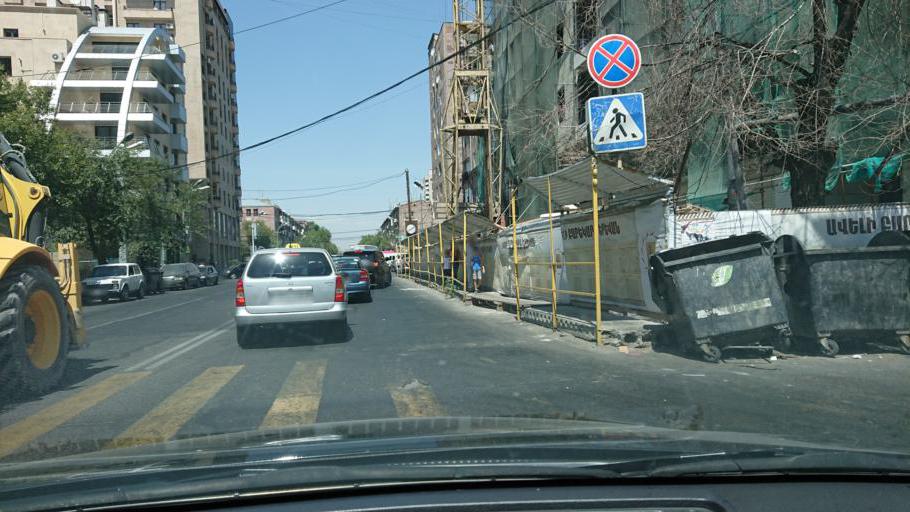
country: AM
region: Yerevan
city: Yerevan
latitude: 40.1997
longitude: 44.5009
